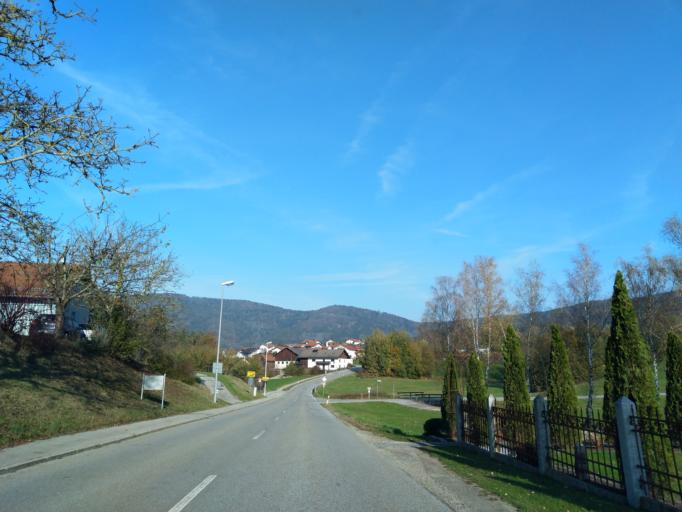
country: DE
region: Bavaria
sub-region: Lower Bavaria
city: Lalling
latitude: 48.8469
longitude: 13.1401
